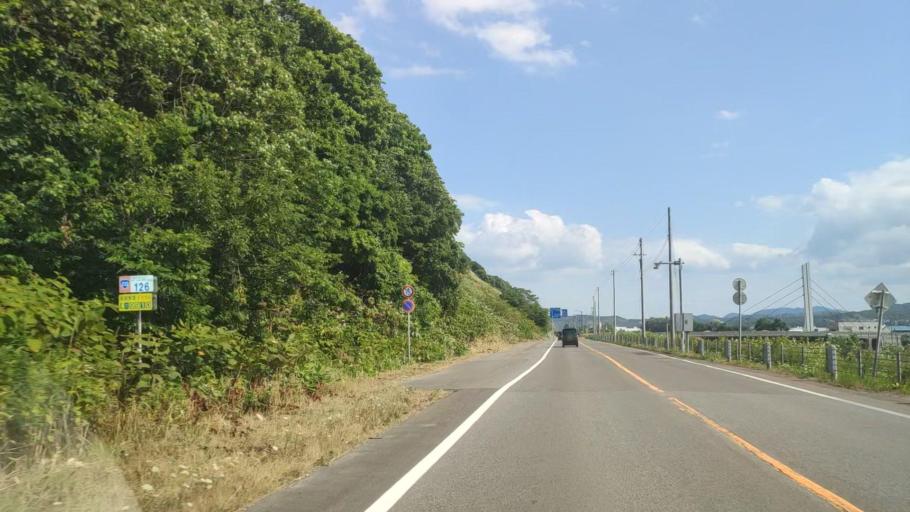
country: JP
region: Hokkaido
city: Rumoi
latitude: 43.9495
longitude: 141.6486
